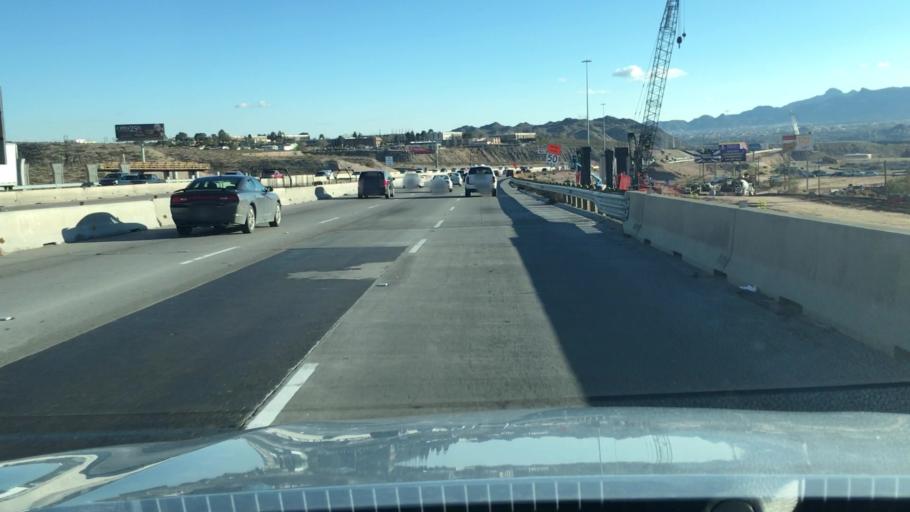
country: US
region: Texas
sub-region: El Paso County
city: El Paso
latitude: 31.8030
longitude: -106.5212
